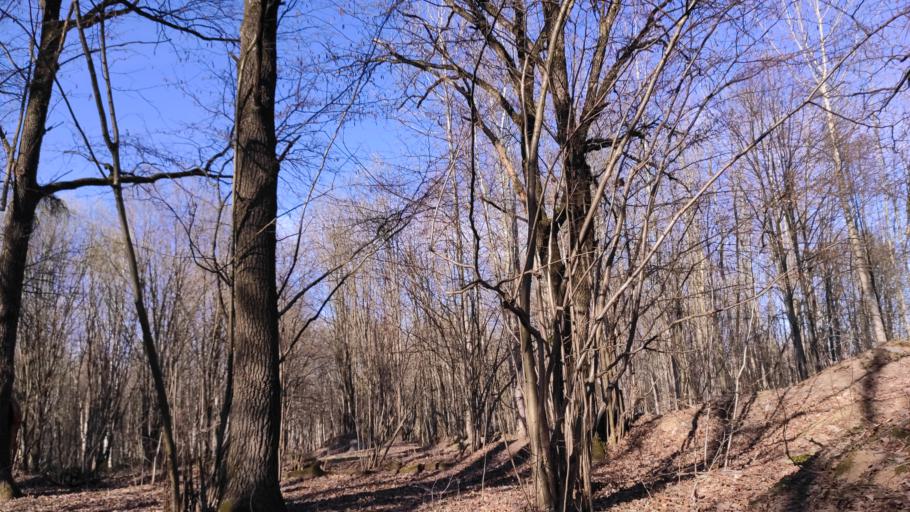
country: BY
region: Minsk
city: Novoye Medvezhino
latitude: 53.8889
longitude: 27.4587
